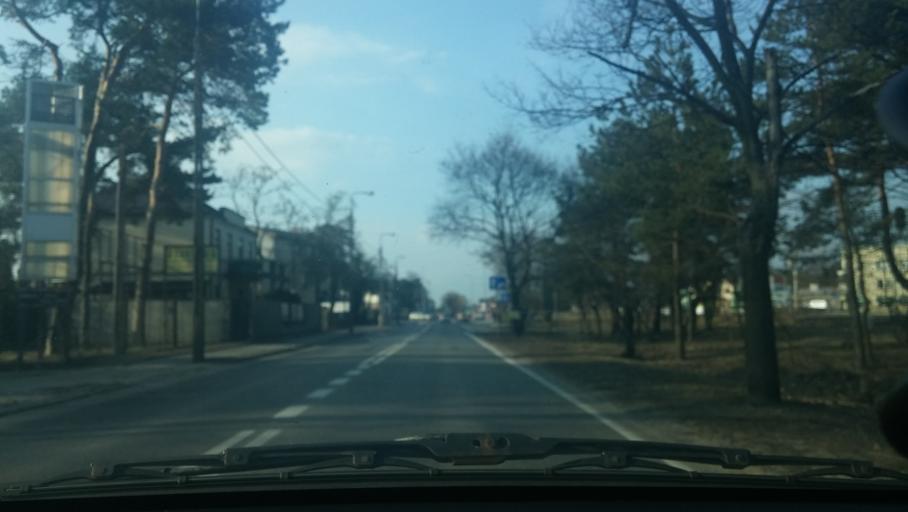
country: PL
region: Masovian Voivodeship
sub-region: Warszawa
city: Wawer
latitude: 52.1826
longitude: 21.1899
